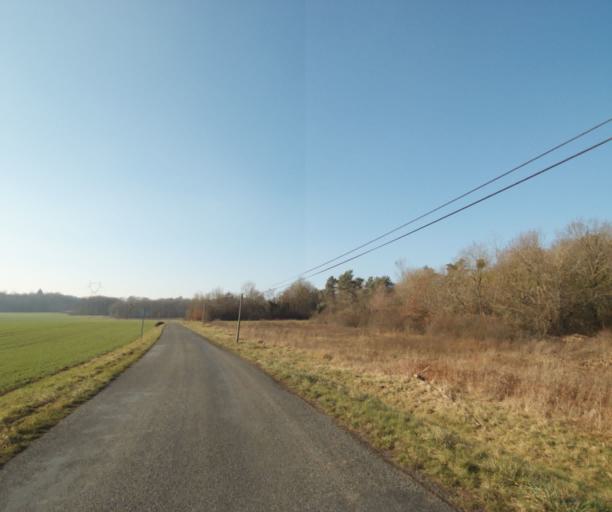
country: FR
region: Champagne-Ardenne
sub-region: Departement de la Haute-Marne
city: Wassy
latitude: 48.5191
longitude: 4.9806
